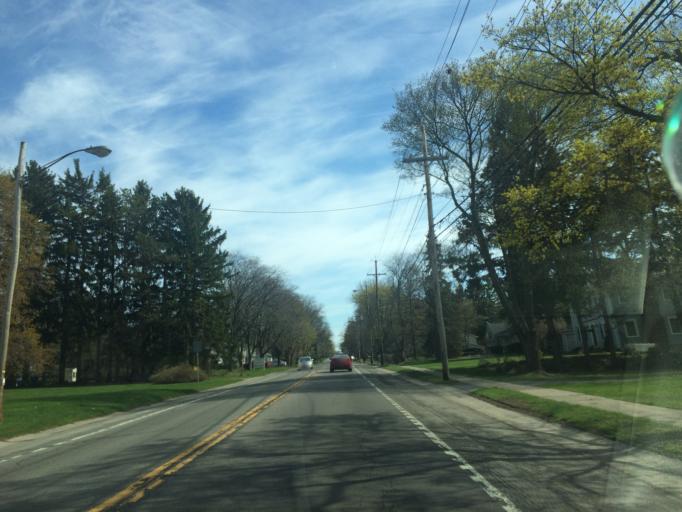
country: US
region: New York
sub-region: Monroe County
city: Webster
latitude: 43.2060
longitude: -77.4303
